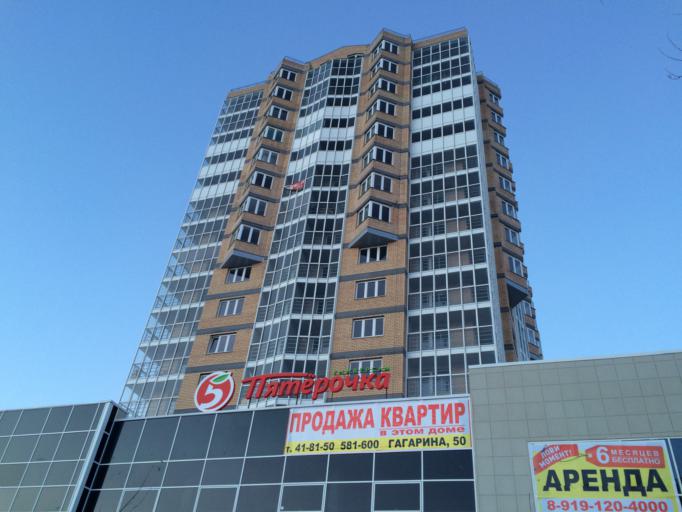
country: RU
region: Chelyabinsk
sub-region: Gorod Magnitogorsk
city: Magnitogorsk
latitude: 53.3983
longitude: 58.9847
